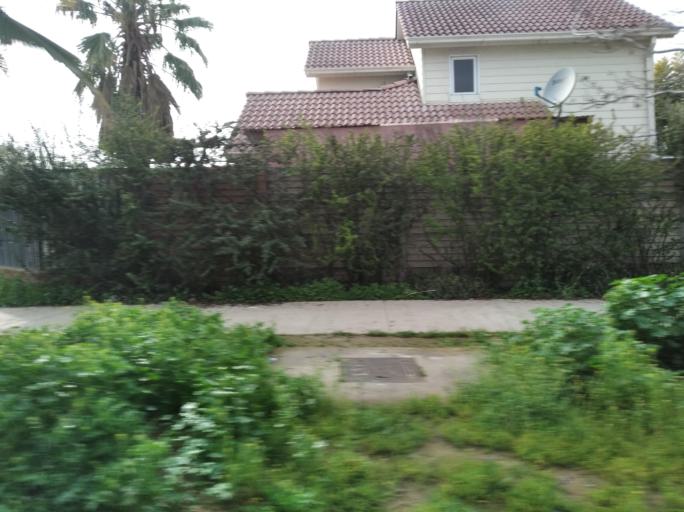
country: CL
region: Santiago Metropolitan
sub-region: Provincia de Chacabuco
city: Lampa
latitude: -33.2972
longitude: -70.8851
